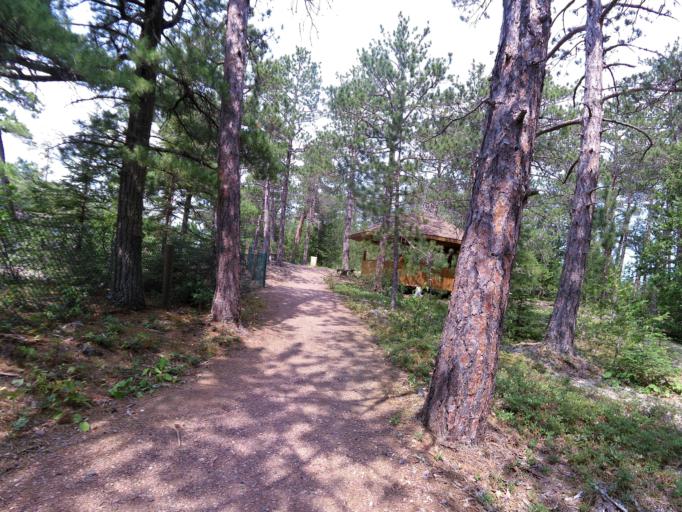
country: CA
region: Ontario
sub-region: Thunder Bay District
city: Thunder Bay
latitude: 48.7989
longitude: -88.6177
